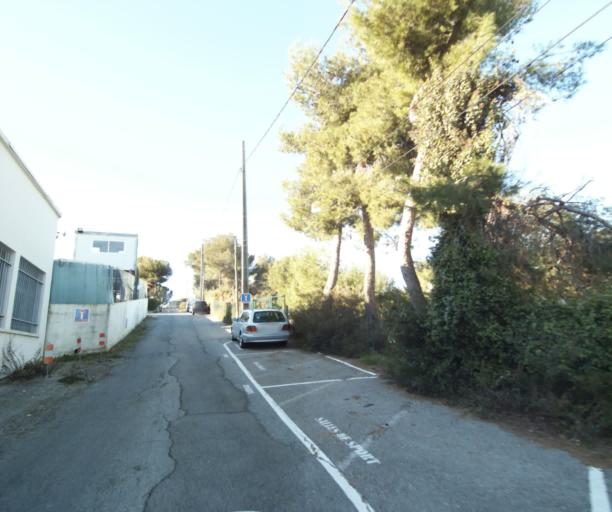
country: FR
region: Provence-Alpes-Cote d'Azur
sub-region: Departement des Alpes-Maritimes
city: Biot
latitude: 43.6006
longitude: 7.0786
